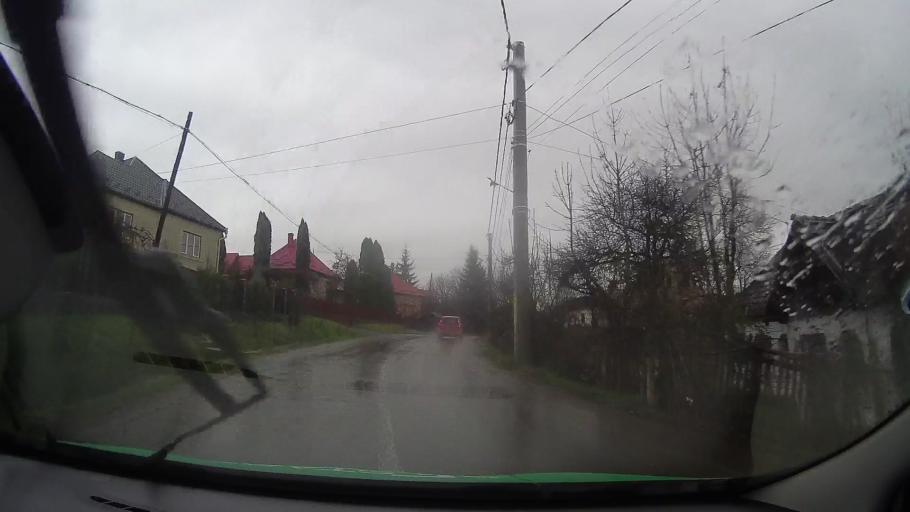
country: RO
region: Mures
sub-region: Comuna Vatava
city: Vatava
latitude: 46.9394
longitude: 24.7670
